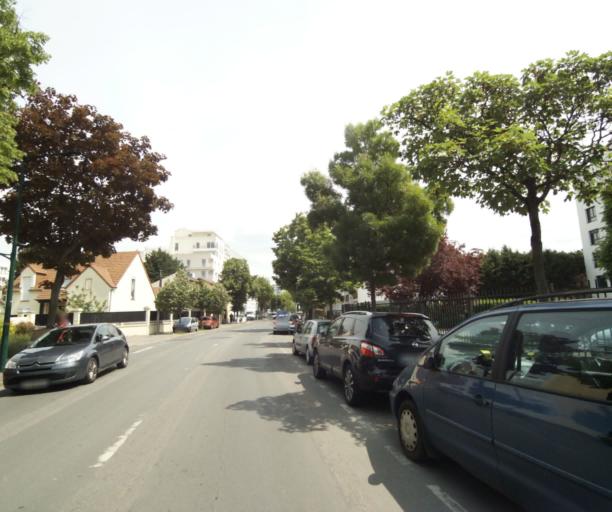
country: FR
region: Ile-de-France
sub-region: Departement des Hauts-de-Seine
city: Colombes
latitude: 48.9254
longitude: 2.2408
